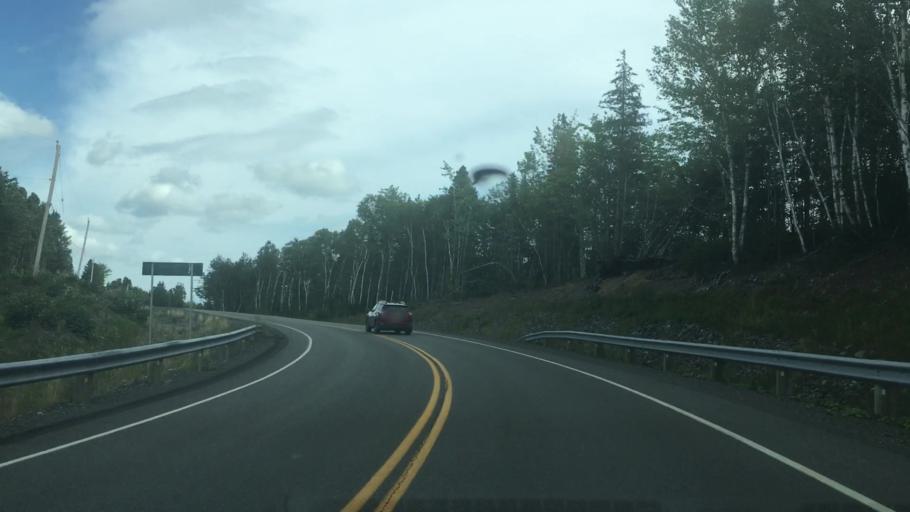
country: CA
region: Nova Scotia
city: Sydney Mines
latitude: 46.3082
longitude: -60.6172
